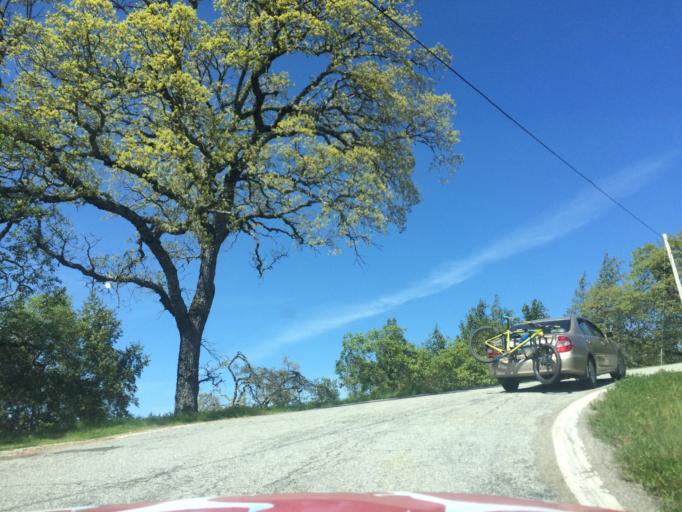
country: US
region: California
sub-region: Santa Clara County
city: Morgan Hill
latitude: 37.1842
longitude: -121.5575
